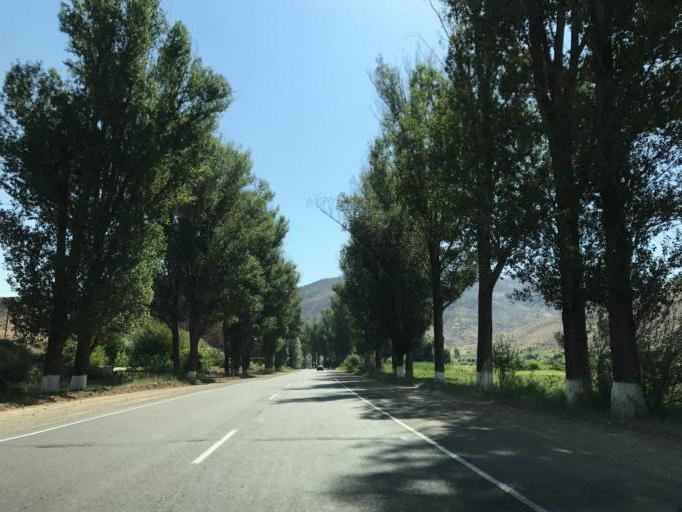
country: AM
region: Vayots' Dzori Marz
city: Getap'
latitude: 39.7371
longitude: 45.2986
